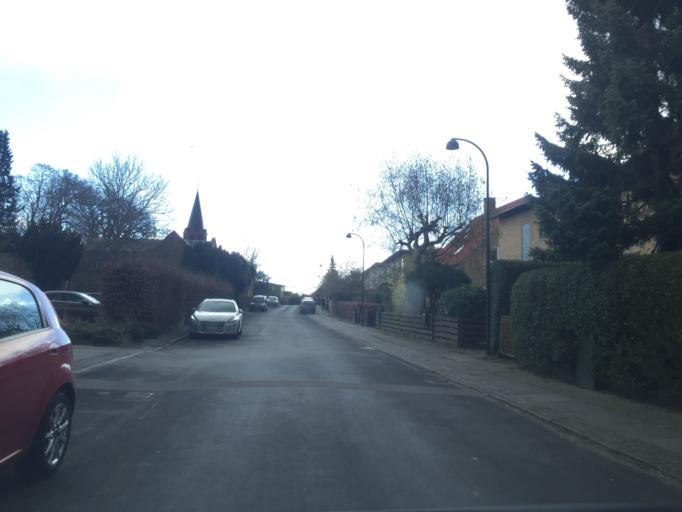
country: DK
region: Capital Region
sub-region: Gentofte Kommune
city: Charlottenlund
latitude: 55.7617
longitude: 12.5670
